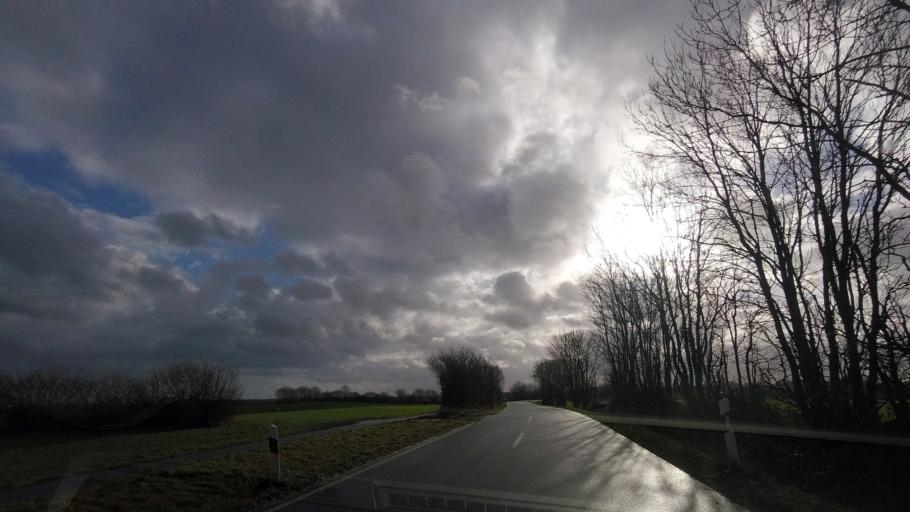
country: DE
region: Schleswig-Holstein
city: Grodersby
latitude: 54.6469
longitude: 9.9176
